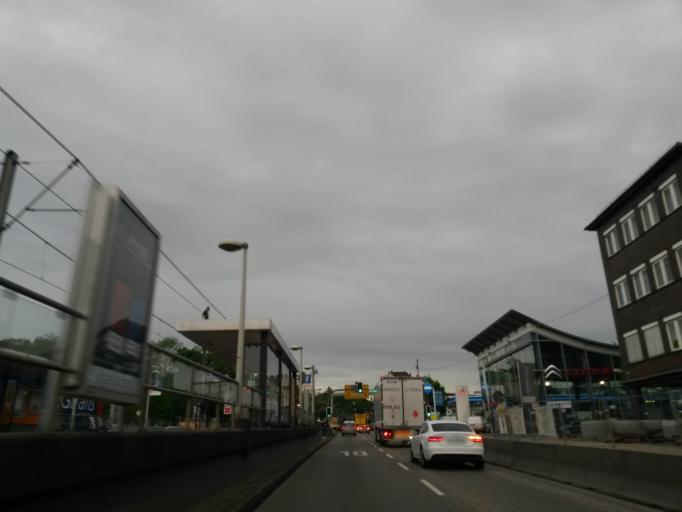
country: DE
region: Baden-Wuerttemberg
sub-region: Regierungsbezirk Stuttgart
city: Stuttgart-Ost
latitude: 48.8073
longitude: 9.1950
